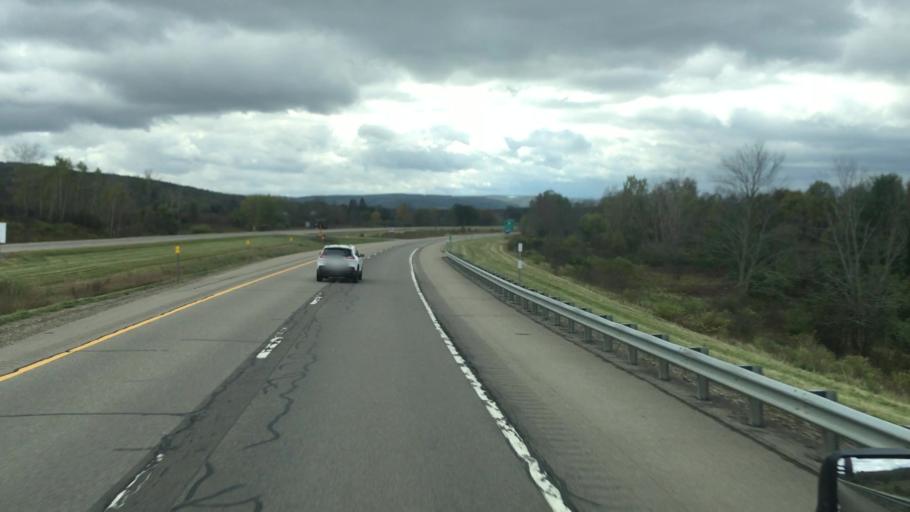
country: US
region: New York
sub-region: Allegany County
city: Belmont
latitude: 42.2892
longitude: -78.0318
